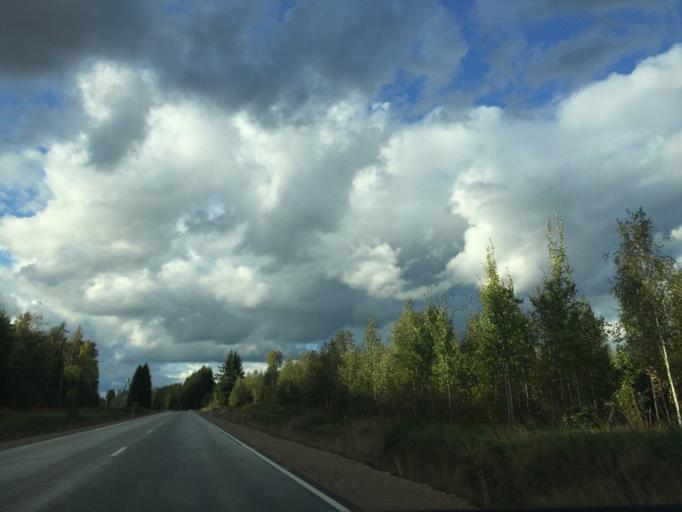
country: LV
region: Ligatne
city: Ligatne
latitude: 57.1499
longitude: 25.0735
